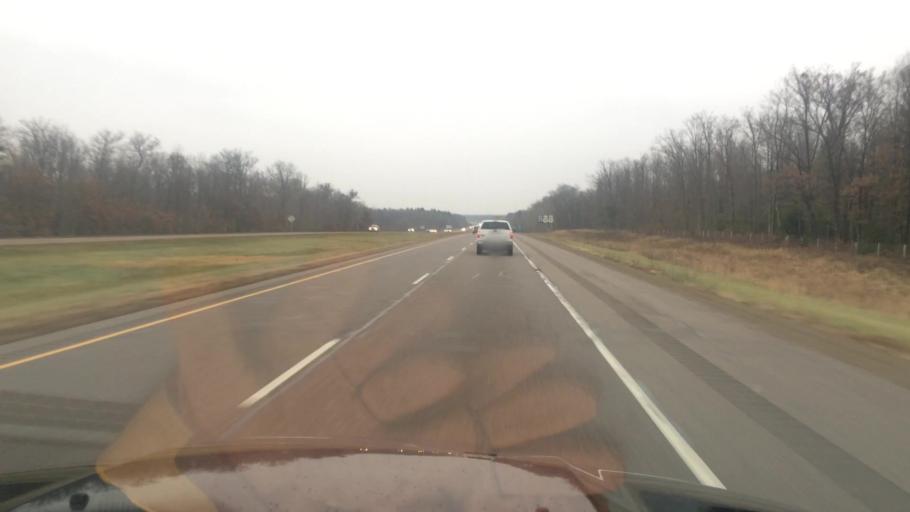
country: US
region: Wisconsin
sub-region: Portage County
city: Stevens Point
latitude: 44.5925
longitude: -89.6125
